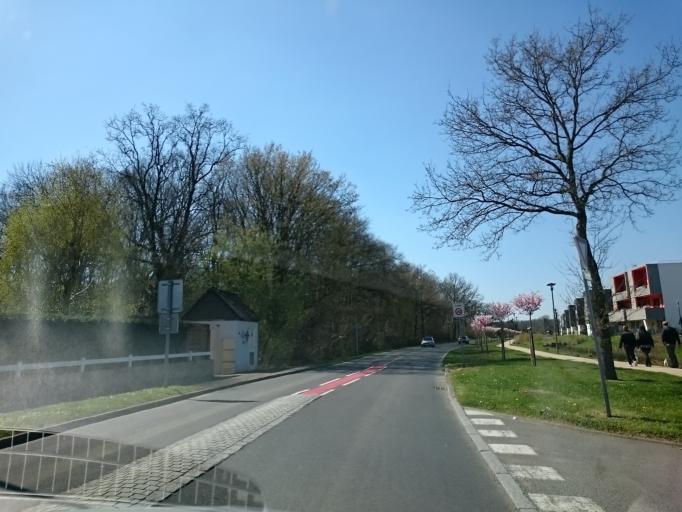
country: FR
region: Brittany
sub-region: Departement d'Ille-et-Vilaine
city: Orgeres
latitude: 48.0026
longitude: -1.6704
